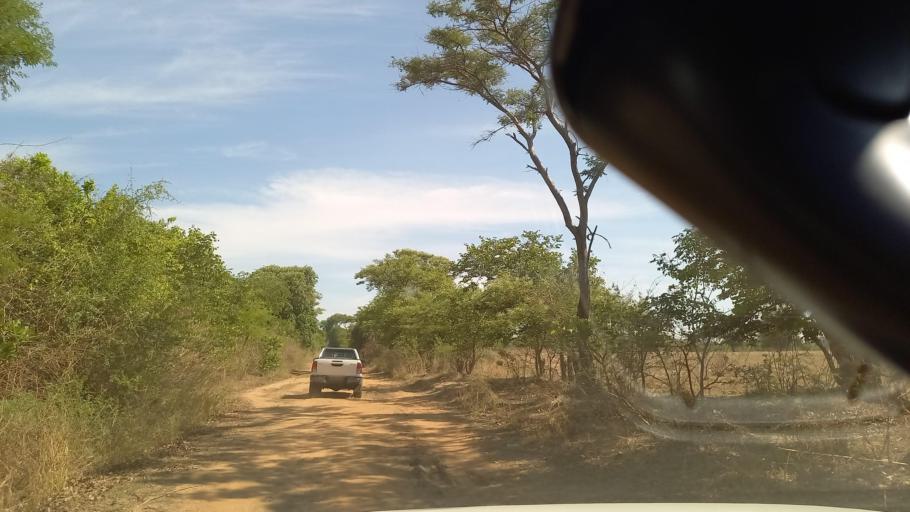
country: ZM
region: Southern
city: Mazabuka
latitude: -16.0389
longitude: 27.6221
